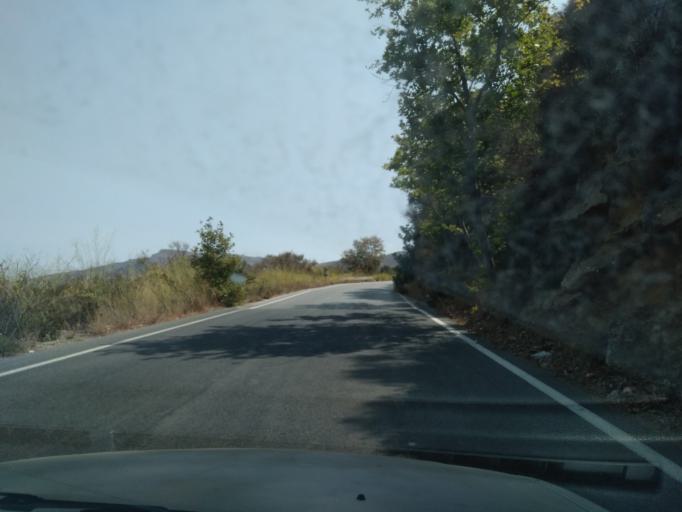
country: GR
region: Crete
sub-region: Nomos Lasithiou
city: Siteia
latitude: 35.1402
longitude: 26.0734
